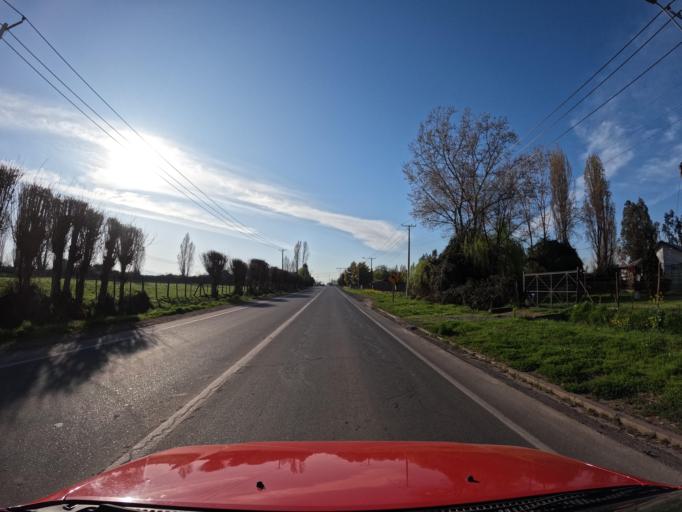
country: CL
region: Maule
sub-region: Provincia de Curico
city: Teno
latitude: -34.9014
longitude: -71.0561
